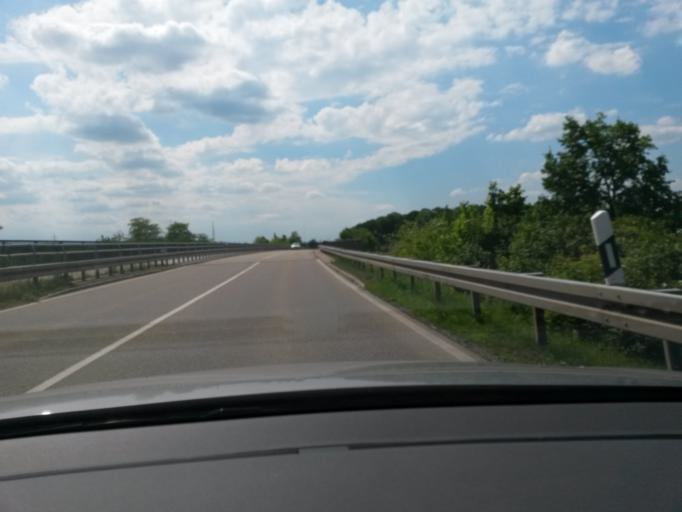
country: DE
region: Baden-Wuerttemberg
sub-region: Regierungsbezirk Stuttgart
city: Vaihingen an der Enz
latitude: 48.9532
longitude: 8.9515
